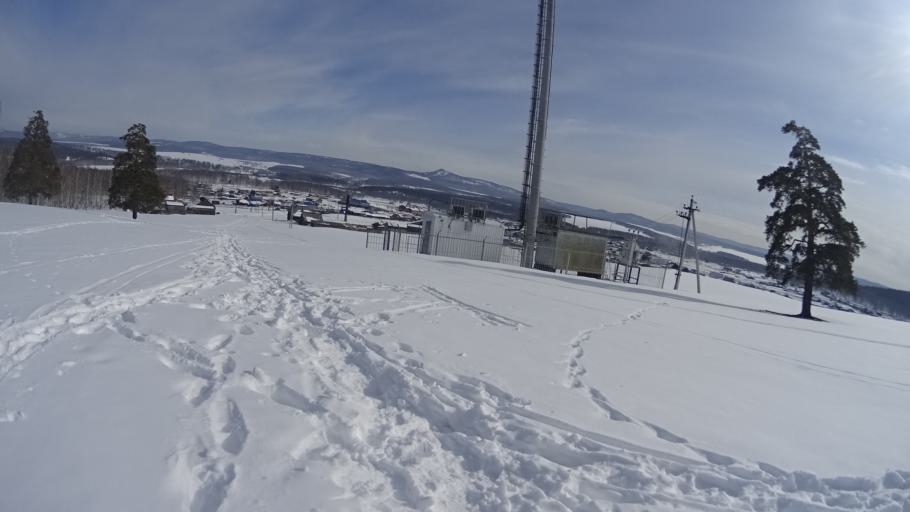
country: RU
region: Bashkortostan
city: Lomovka
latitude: 53.8080
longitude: 58.1954
